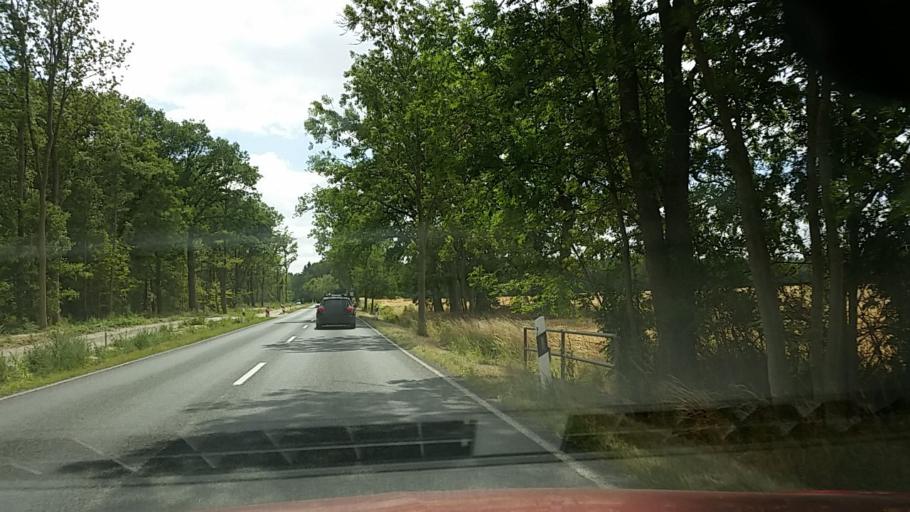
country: DE
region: Lower Saxony
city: Gross Twulpstedt
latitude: 52.3719
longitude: 10.8488
